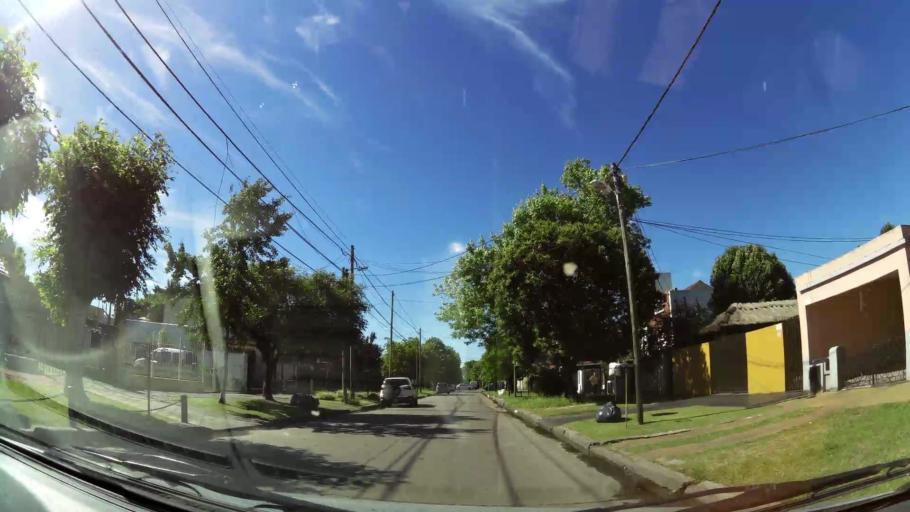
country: AR
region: Buenos Aires
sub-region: Partido de Lomas de Zamora
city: Lomas de Zamora
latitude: -34.7431
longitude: -58.4171
